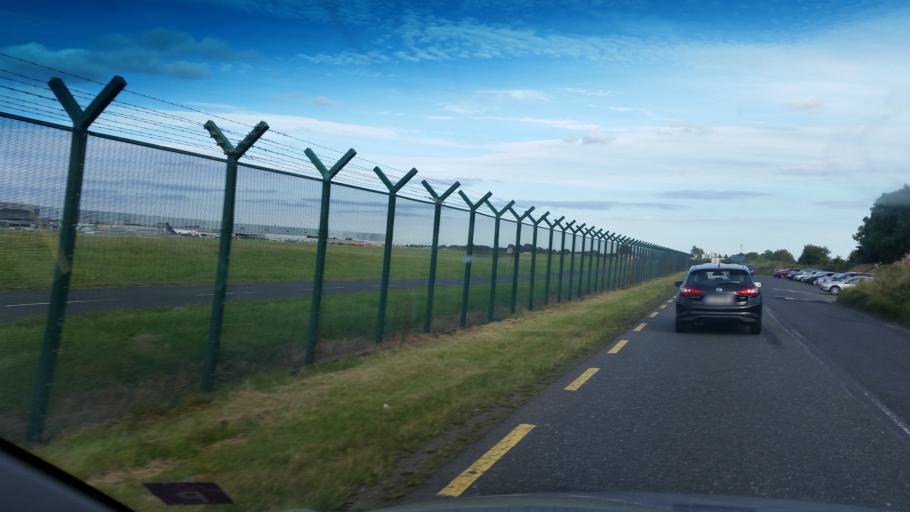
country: IE
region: Leinster
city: Ballymun
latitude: 53.4186
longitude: -6.2539
